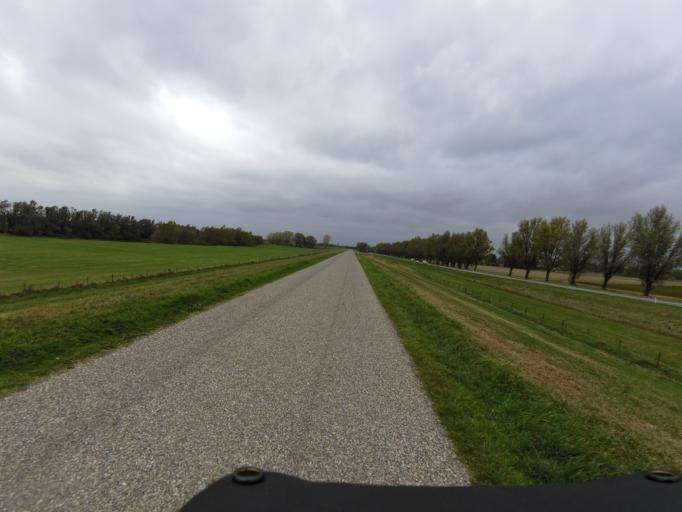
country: NL
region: Gelderland
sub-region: Gemeente Zevenaar
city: Zevenaar
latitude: 51.8758
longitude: 6.1010
